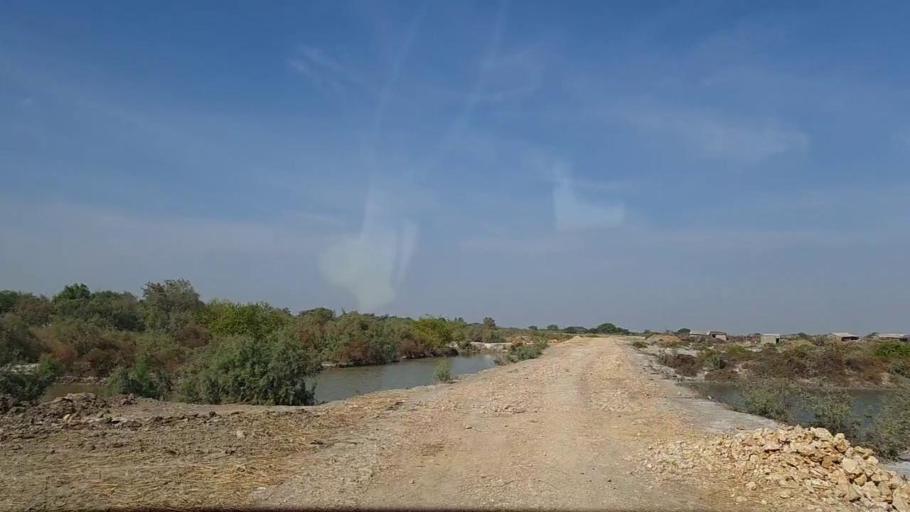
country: PK
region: Sindh
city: Daro Mehar
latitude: 24.7067
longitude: 68.1503
